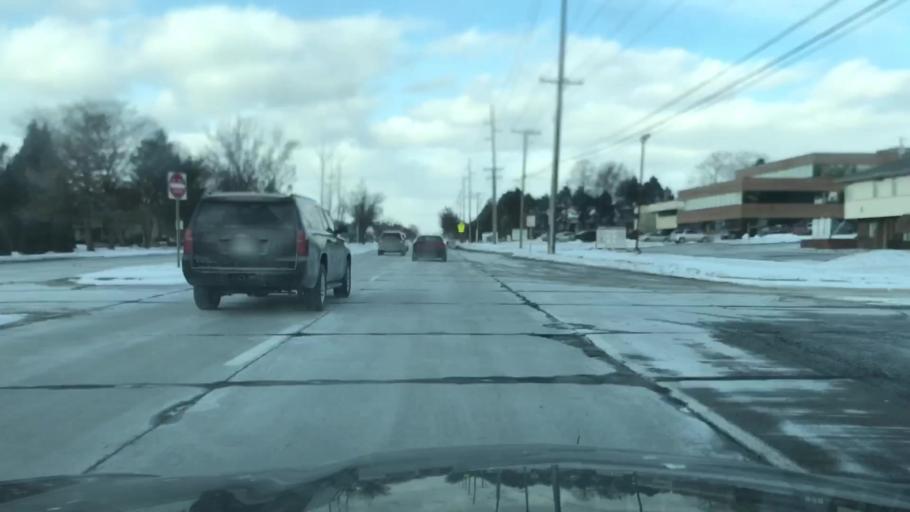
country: US
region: Michigan
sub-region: Oakland County
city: Rochester Hills
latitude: 42.6727
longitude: -83.1532
